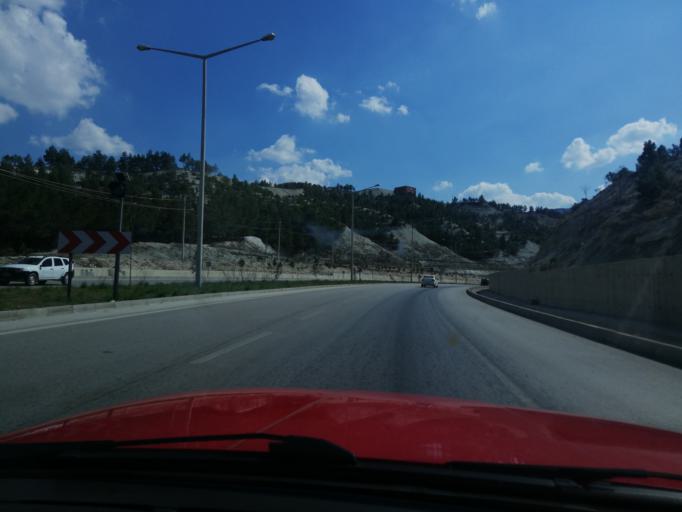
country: TR
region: Burdur
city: Burdur
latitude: 37.7162
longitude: 30.2985
